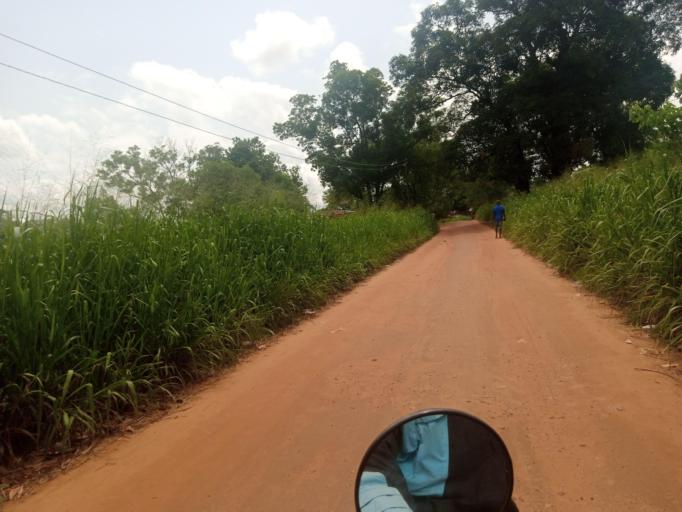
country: SL
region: Southern Province
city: Bo
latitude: 7.9632
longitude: -11.7488
